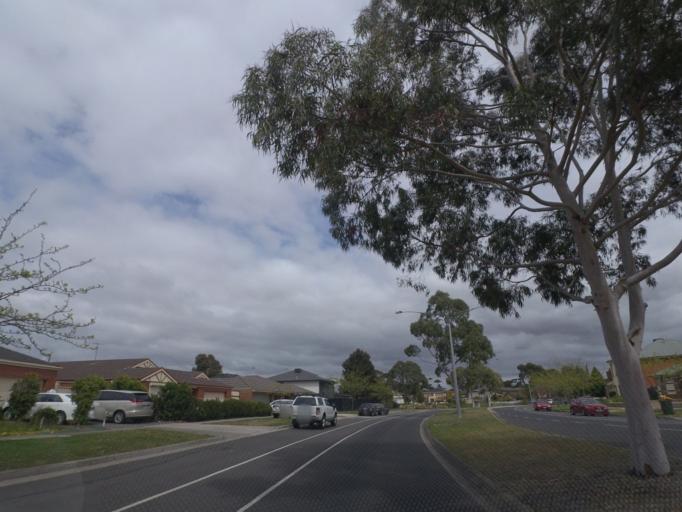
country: AU
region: Victoria
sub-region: Brimbank
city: Deer Park
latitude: -37.7601
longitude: 144.7807
